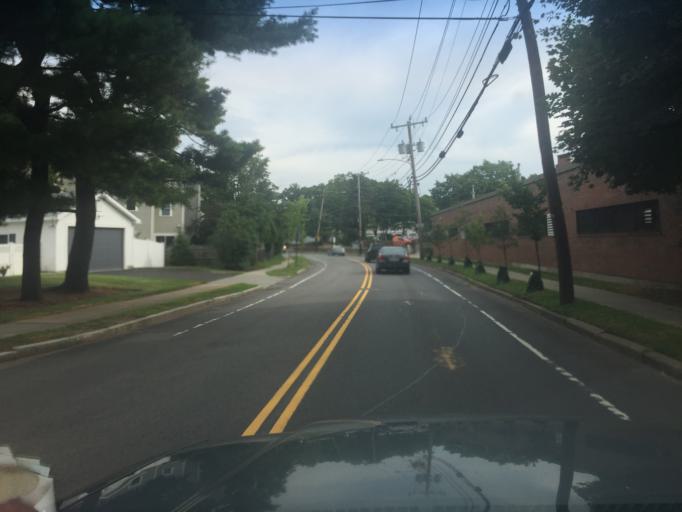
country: US
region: Massachusetts
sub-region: Middlesex County
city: Newton
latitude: 42.3156
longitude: -71.2144
